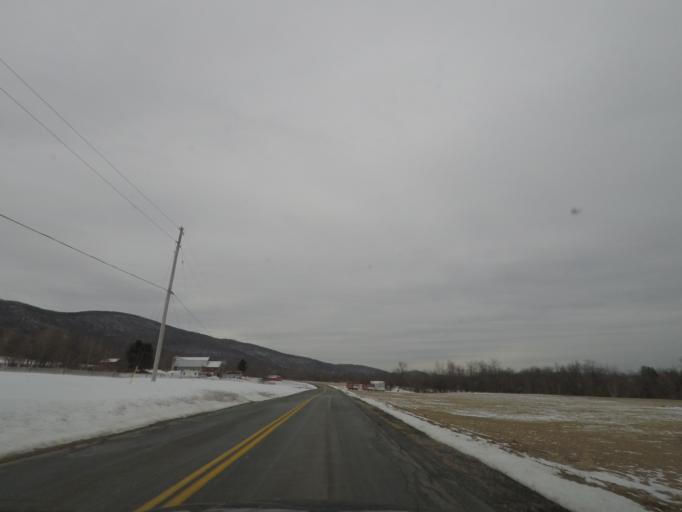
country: US
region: Massachusetts
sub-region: Berkshire County
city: Lanesborough
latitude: 42.5899
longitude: -73.3556
